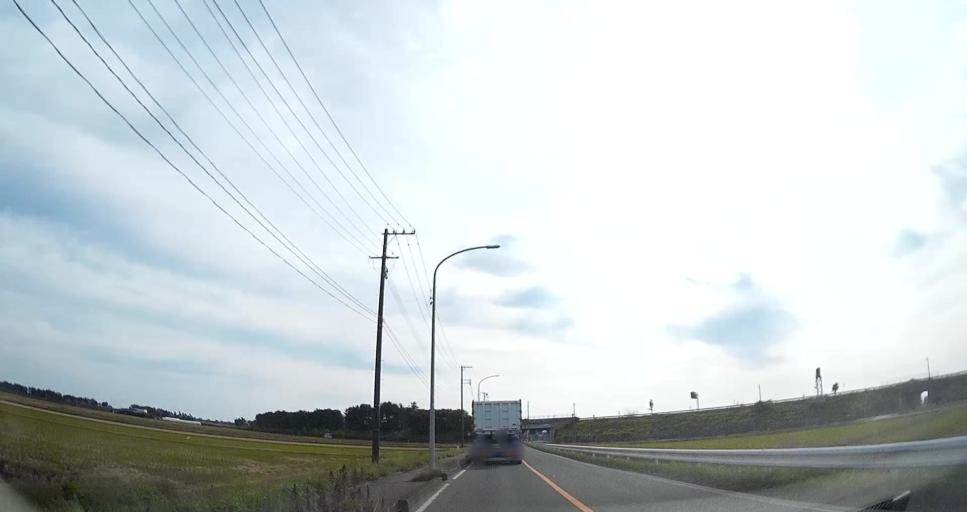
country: JP
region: Miyagi
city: Sendai
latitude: 38.2096
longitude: 140.9367
